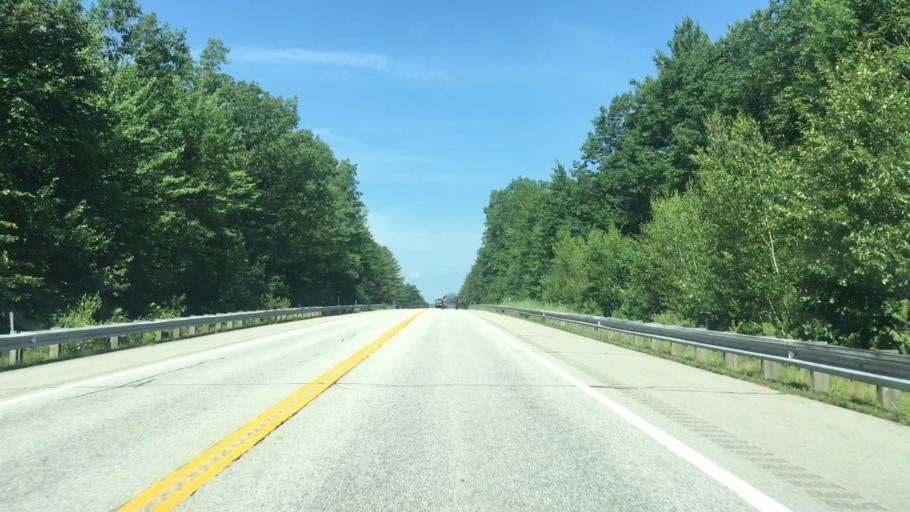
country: US
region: New Hampshire
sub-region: Merrimack County
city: Henniker
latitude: 43.1814
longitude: -71.7684
